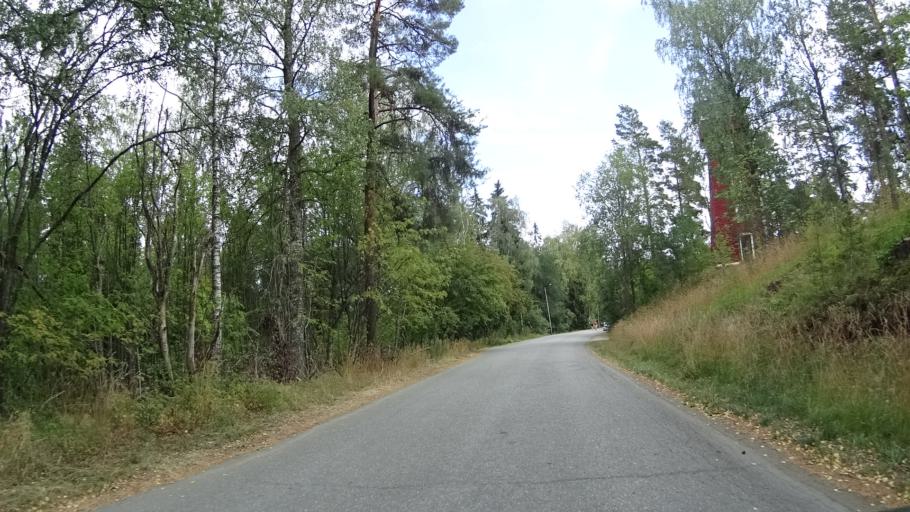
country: FI
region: Pirkanmaa
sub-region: Tampere
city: Kangasala
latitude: 61.4093
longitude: 24.1555
